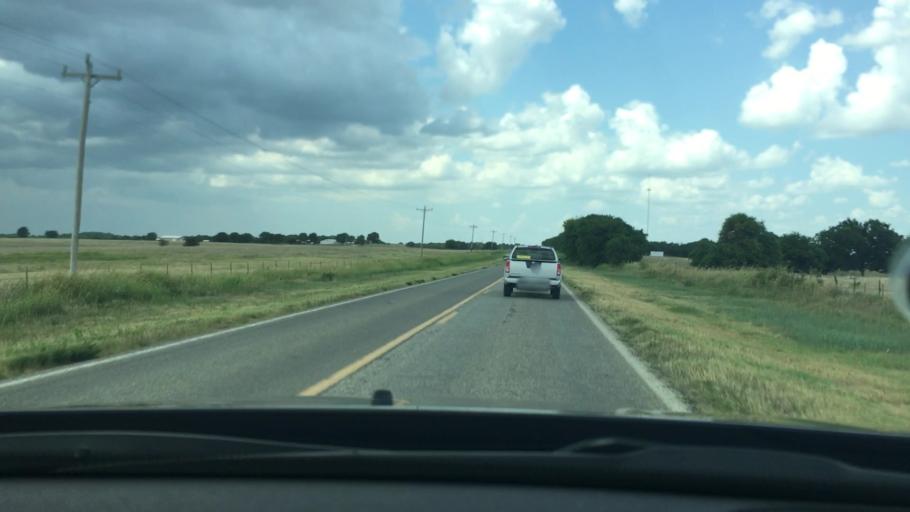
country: US
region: Oklahoma
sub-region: Pontotoc County
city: Ada
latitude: 34.5549
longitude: -96.6347
